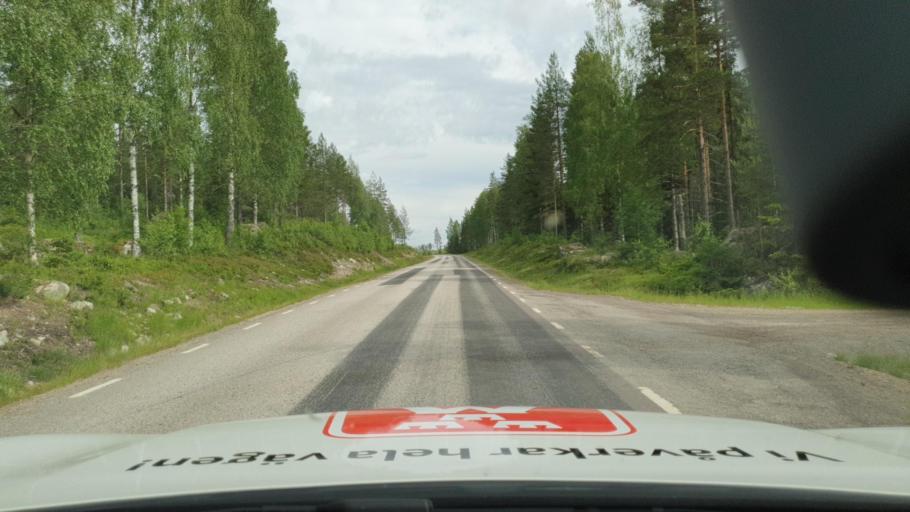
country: NO
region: Hedmark
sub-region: Trysil
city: Innbygda
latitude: 61.0265
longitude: 12.4915
